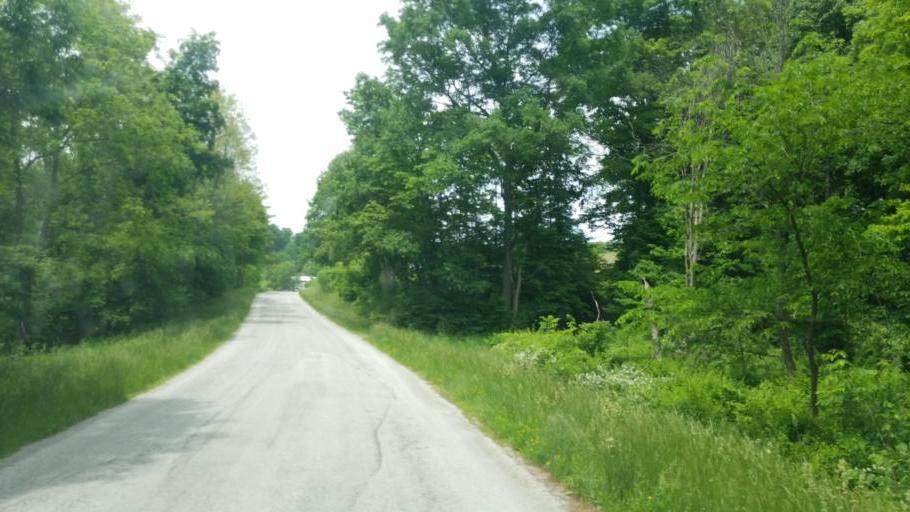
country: US
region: Ohio
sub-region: Coshocton County
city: West Lafayette
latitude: 40.3775
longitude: -81.7833
